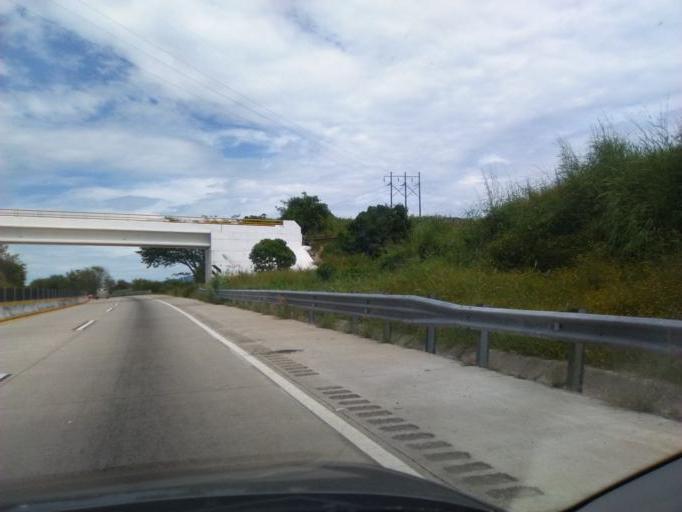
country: MX
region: Guerrero
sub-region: Chilpancingo de los Bravo
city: Julian Blanco (Dos Caminos)
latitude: 17.2252
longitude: -99.5265
